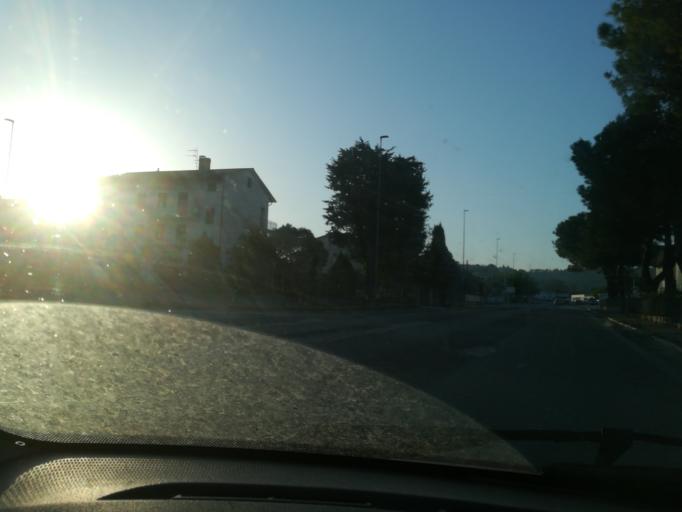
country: IT
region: The Marches
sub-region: Provincia di Macerata
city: Piediripa
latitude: 43.2770
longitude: 13.4921
